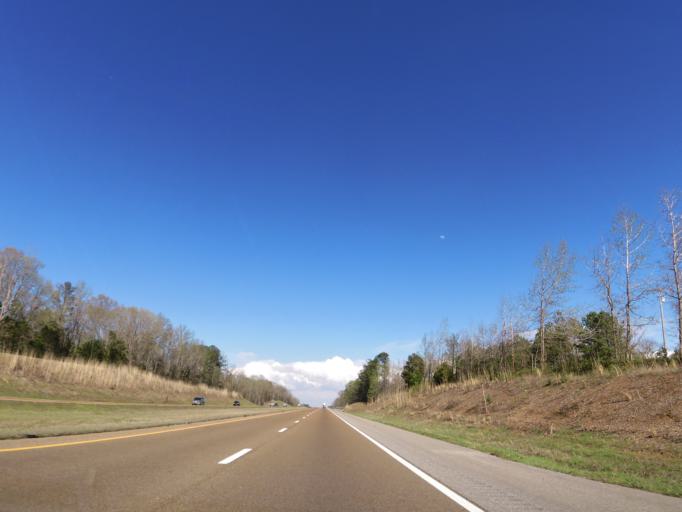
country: US
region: Tennessee
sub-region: Decatur County
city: Parsons
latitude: 35.8196
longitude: -88.1424
